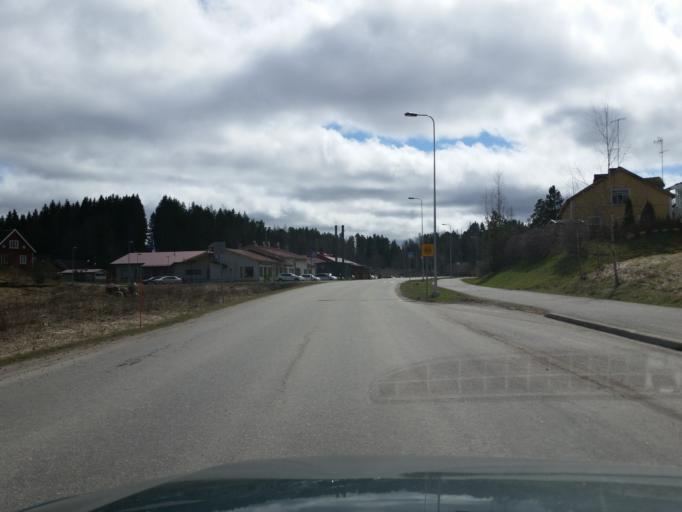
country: FI
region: Uusimaa
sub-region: Helsinki
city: Vihti
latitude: 60.4131
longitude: 24.3302
